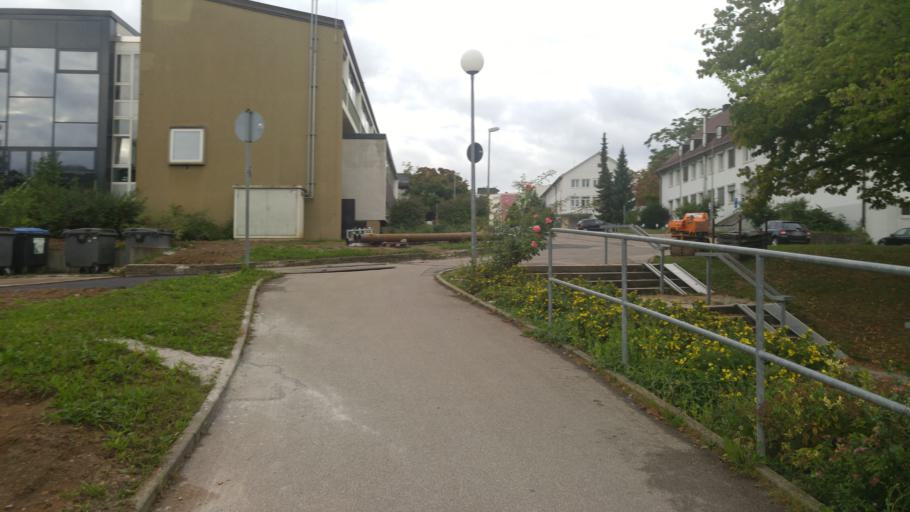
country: DE
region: Baden-Wuerttemberg
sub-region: Regierungsbezirk Stuttgart
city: Leonberg
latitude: 48.7986
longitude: 9.0115
